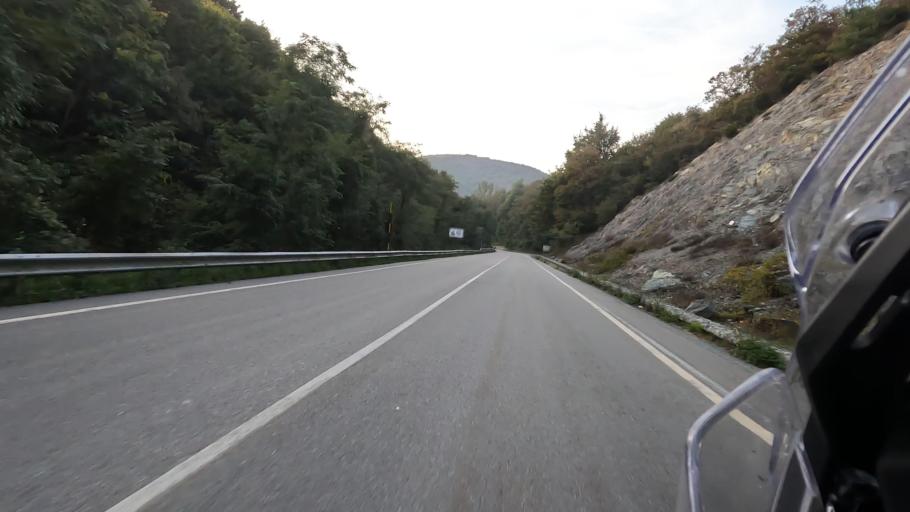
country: IT
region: Liguria
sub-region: Provincia di Savona
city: Osteria dei Cacciatori-Stella
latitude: 44.4444
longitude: 8.4835
